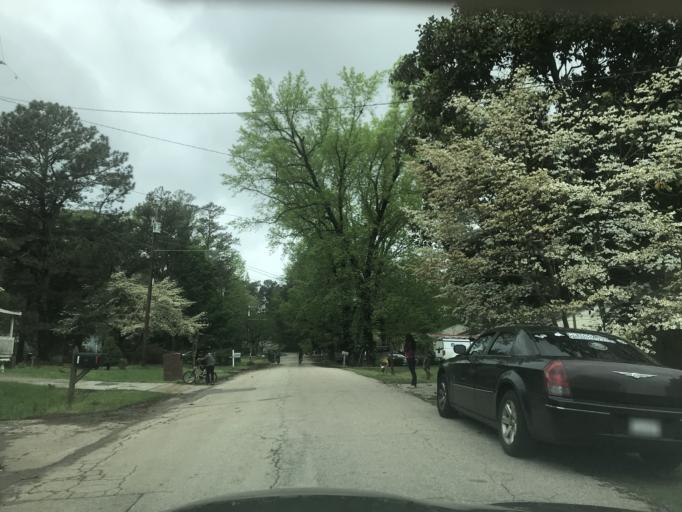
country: US
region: North Carolina
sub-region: Wake County
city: Raleigh
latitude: 35.7493
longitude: -78.6526
